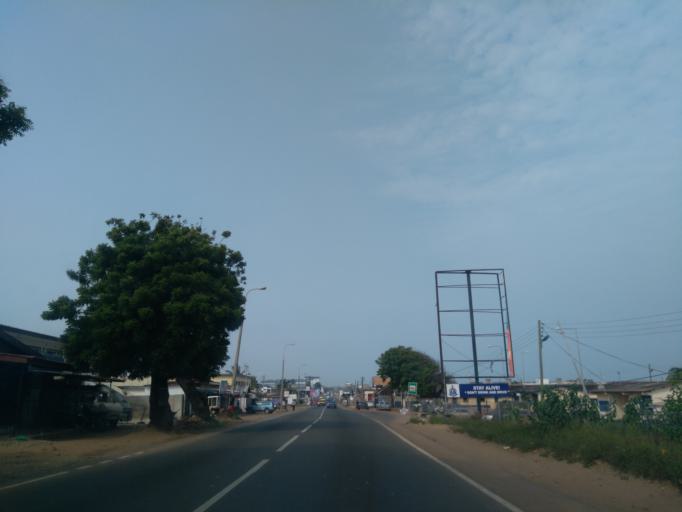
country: GH
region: Greater Accra
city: Accra
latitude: 5.5521
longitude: -0.1786
